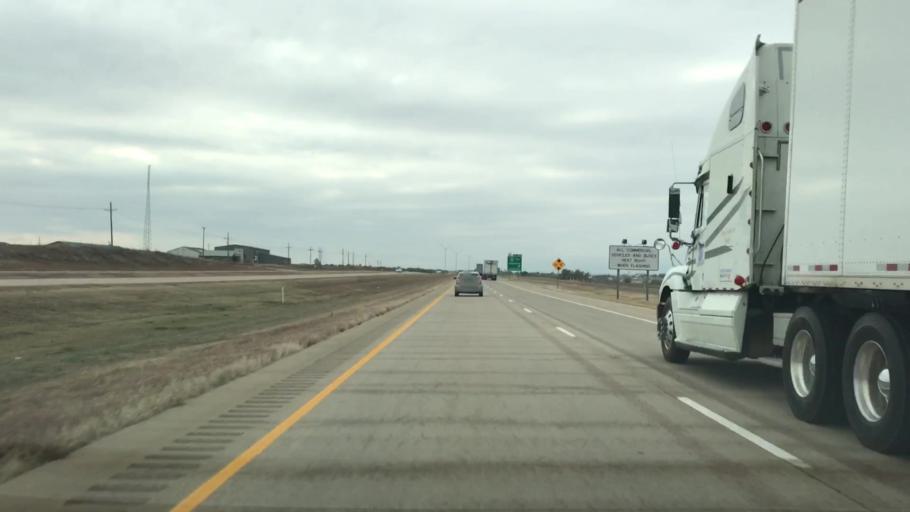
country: US
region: Texas
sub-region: Wheeler County
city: Shamrock
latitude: 35.2270
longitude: -100.2140
